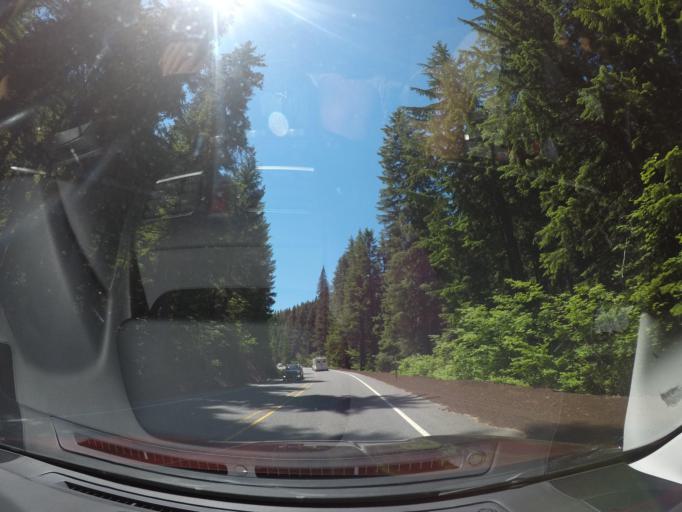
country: US
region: Oregon
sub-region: Deschutes County
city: Sisters
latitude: 44.5446
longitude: -121.9951
